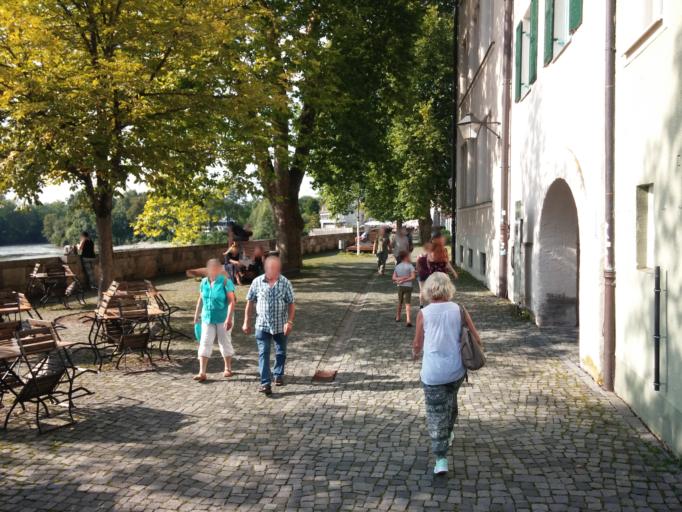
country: DE
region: Bavaria
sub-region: Upper Bavaria
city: Landsberg am Lech
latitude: 48.0478
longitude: 10.8758
